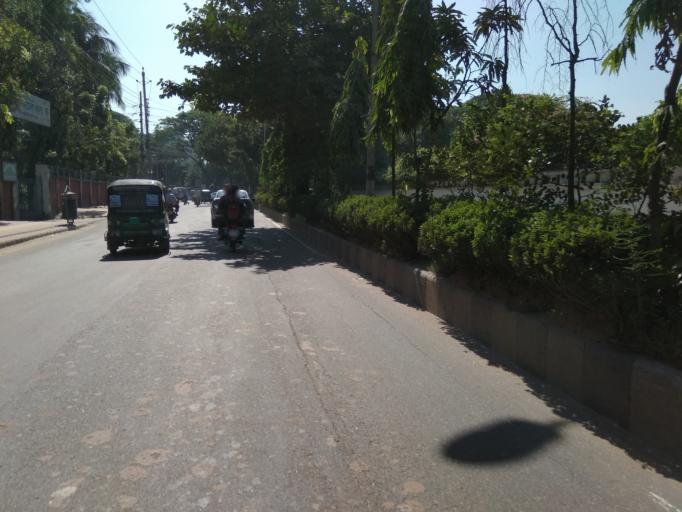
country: BD
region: Dhaka
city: Paltan
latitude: 23.7458
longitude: 90.4040
